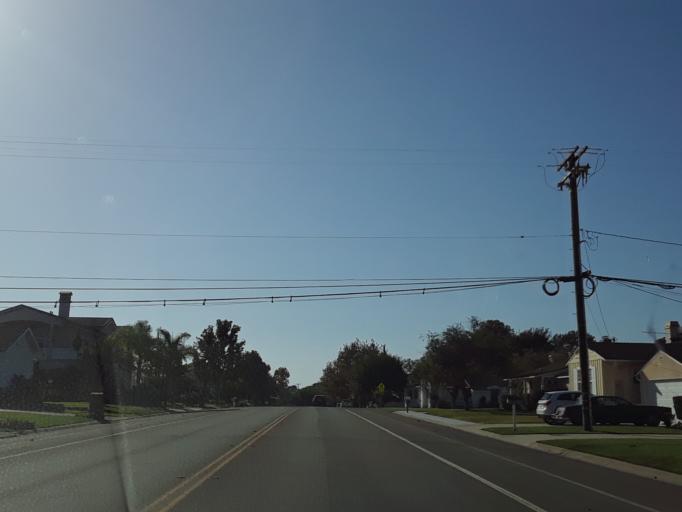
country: US
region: California
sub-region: Orange County
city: Newport Beach
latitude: 33.6178
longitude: -117.9112
